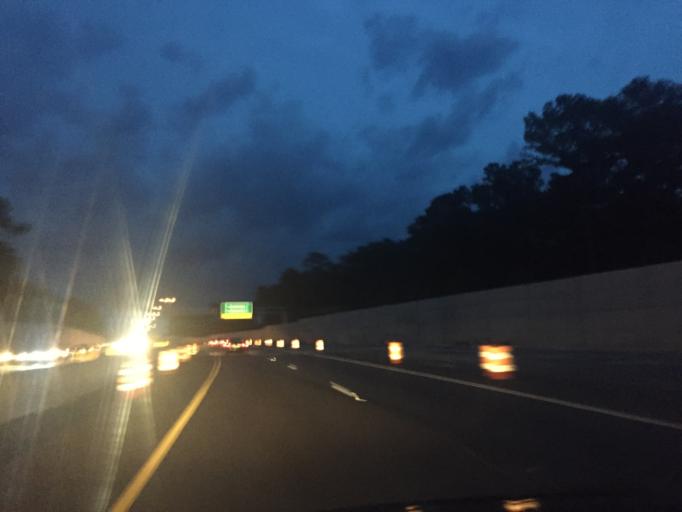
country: US
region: Georgia
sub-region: Chatham County
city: Georgetown
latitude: 31.9850
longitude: -81.2130
